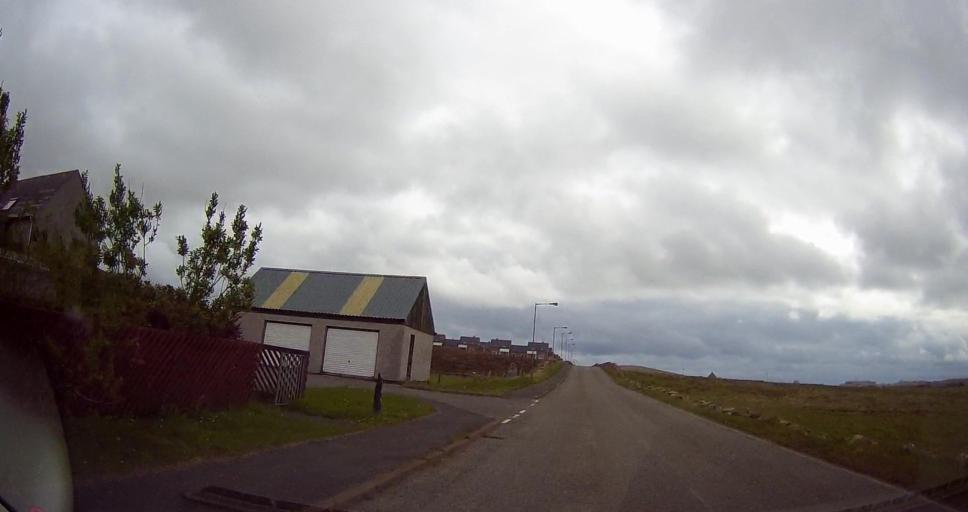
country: GB
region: Scotland
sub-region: Shetland Islands
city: Shetland
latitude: 60.7619
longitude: -0.8699
